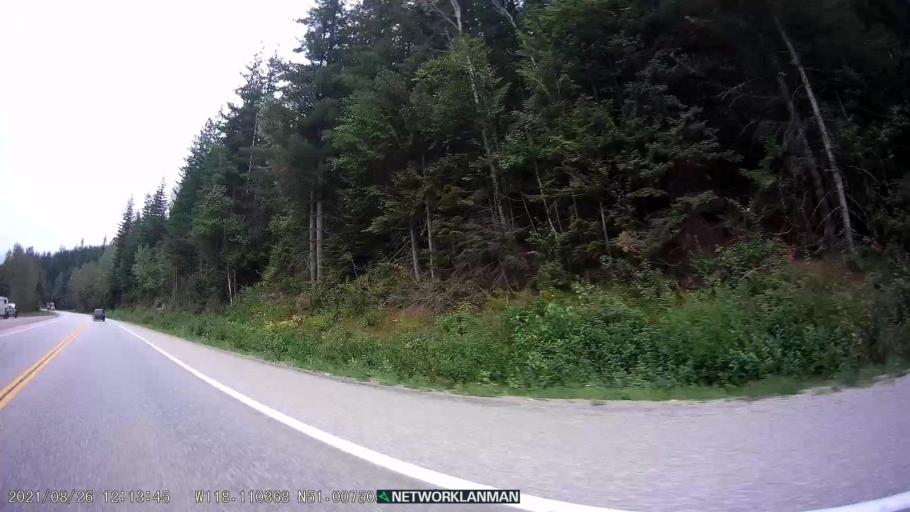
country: CA
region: British Columbia
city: Revelstoke
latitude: 51.0075
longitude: -118.1105
